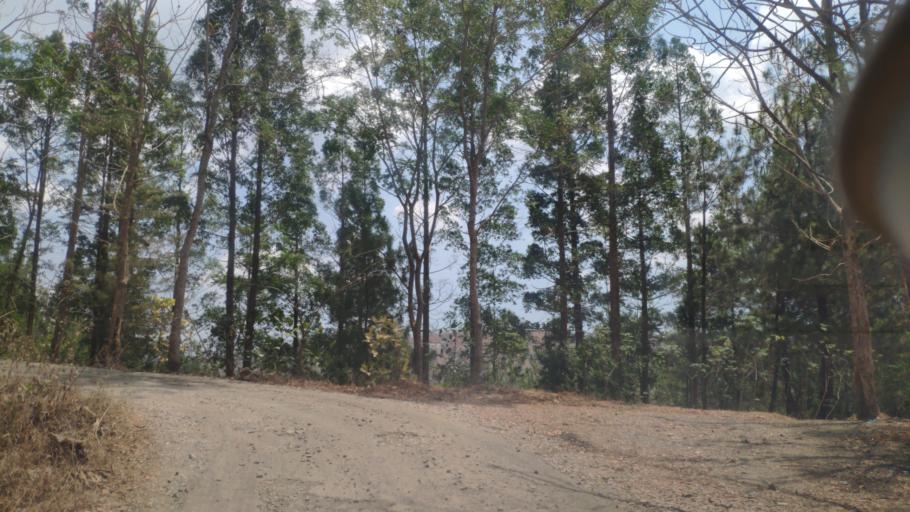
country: ID
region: Central Java
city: Gombong
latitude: -7.4813
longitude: 109.6132
